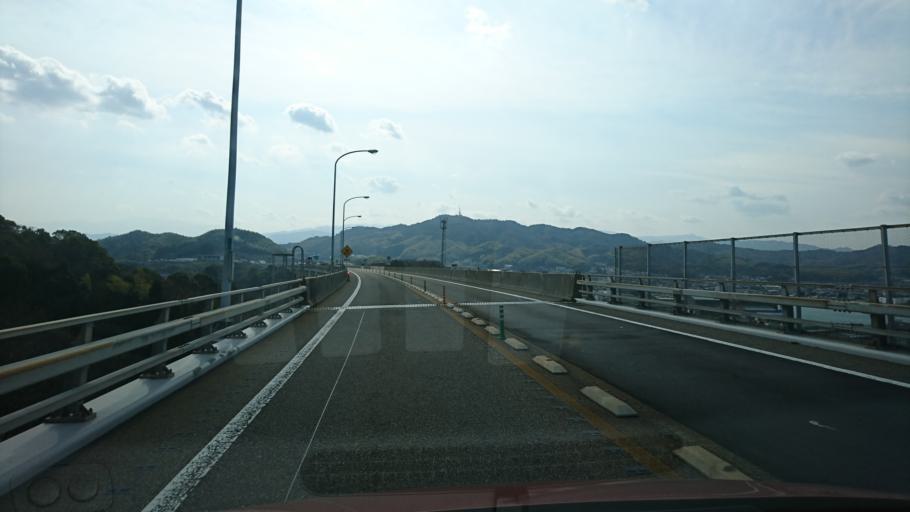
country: JP
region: Hiroshima
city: Takehara
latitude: 34.1093
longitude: 132.9764
